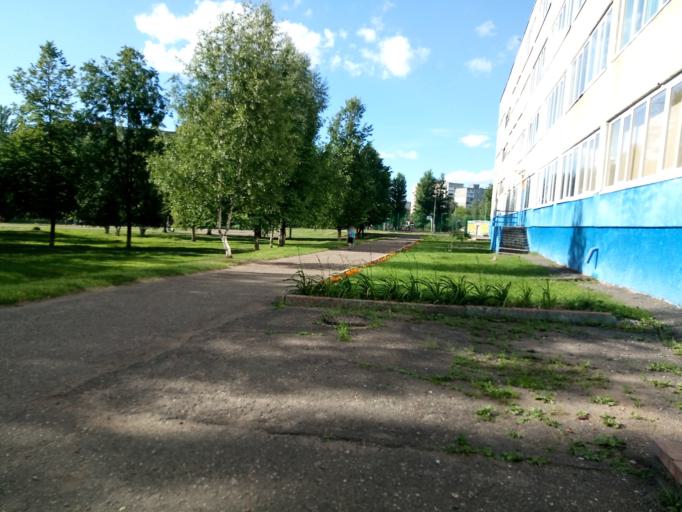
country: RU
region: Jaroslavl
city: Yaroslavl
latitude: 57.6528
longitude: 39.9550
